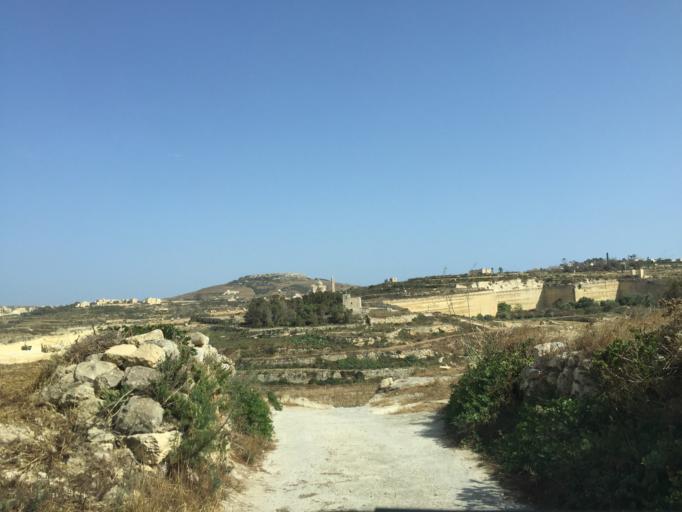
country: MT
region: L-Gharb
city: Gharb
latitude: 36.0701
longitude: 14.2062
